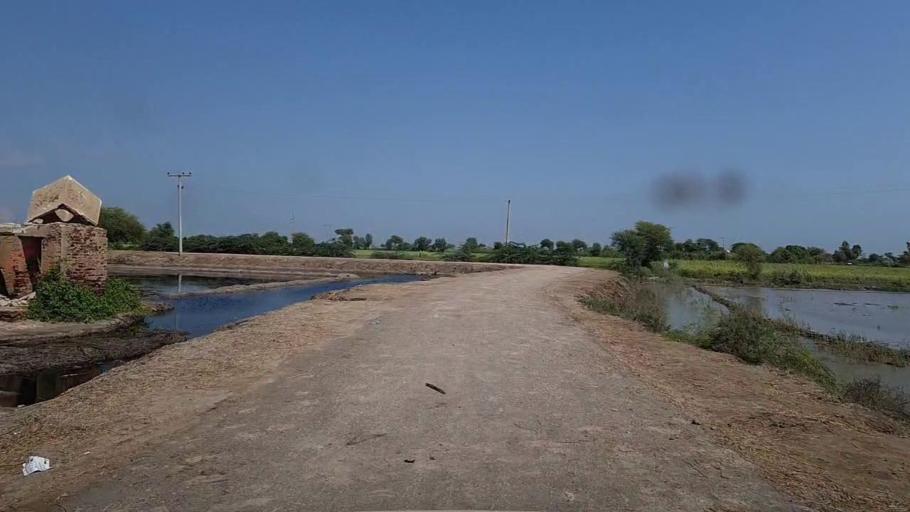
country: PK
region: Sindh
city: Mirpur Batoro
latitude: 24.6447
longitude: 68.4515
